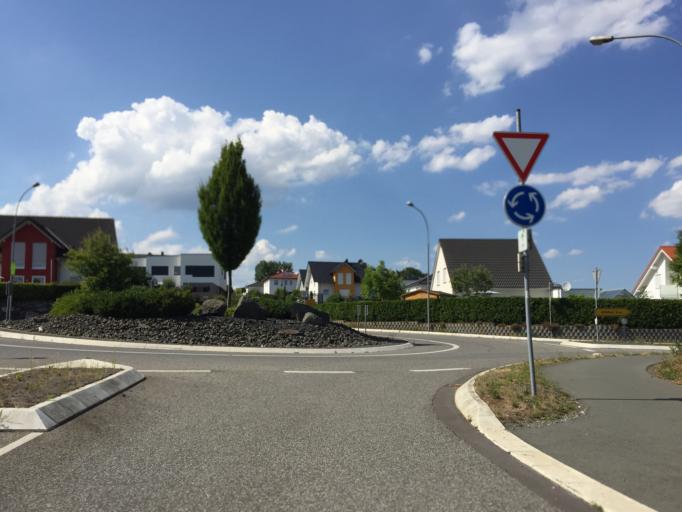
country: DE
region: Hesse
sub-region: Regierungsbezirk Giessen
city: Heuchelheim
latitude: 50.6272
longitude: 8.6422
